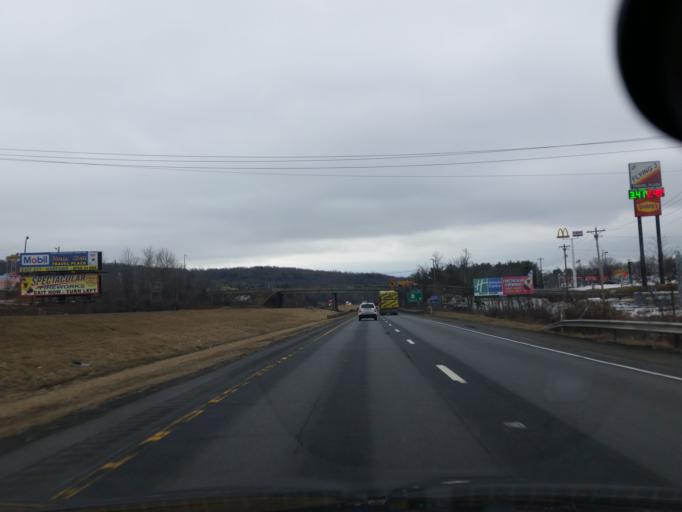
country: US
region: Pennsylvania
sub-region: Susquehanna County
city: Susquehanna
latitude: 41.8262
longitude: -75.6803
